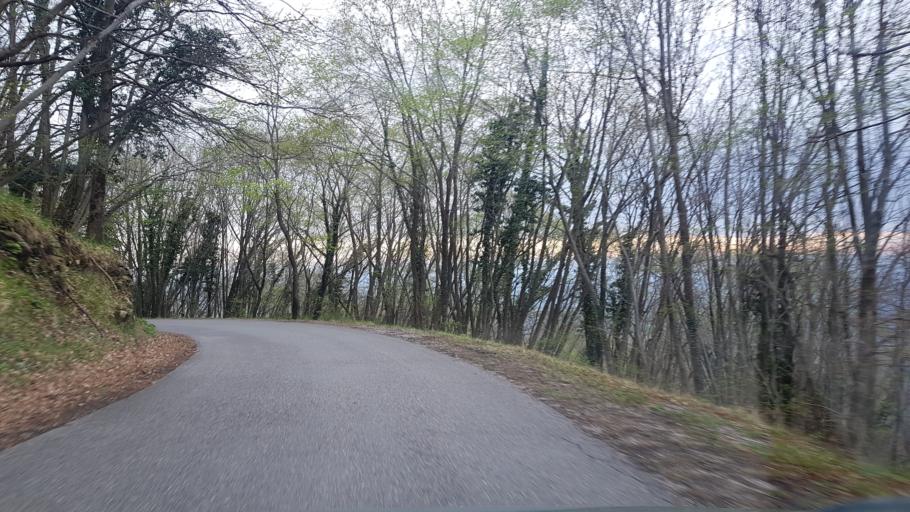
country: SI
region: Kanal
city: Deskle
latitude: 46.0463
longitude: 13.5628
